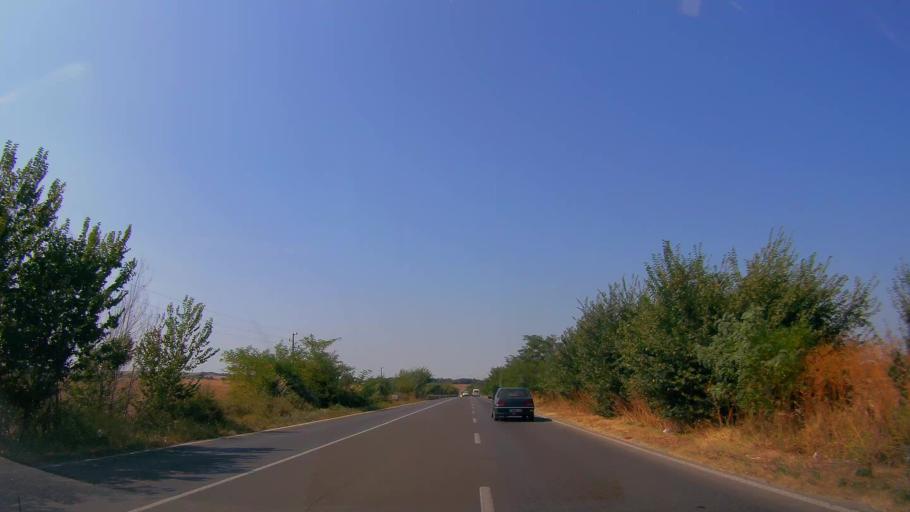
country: BG
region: Ruse
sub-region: Obshtina Vetovo
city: Senovo
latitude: 43.5654
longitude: 26.3345
